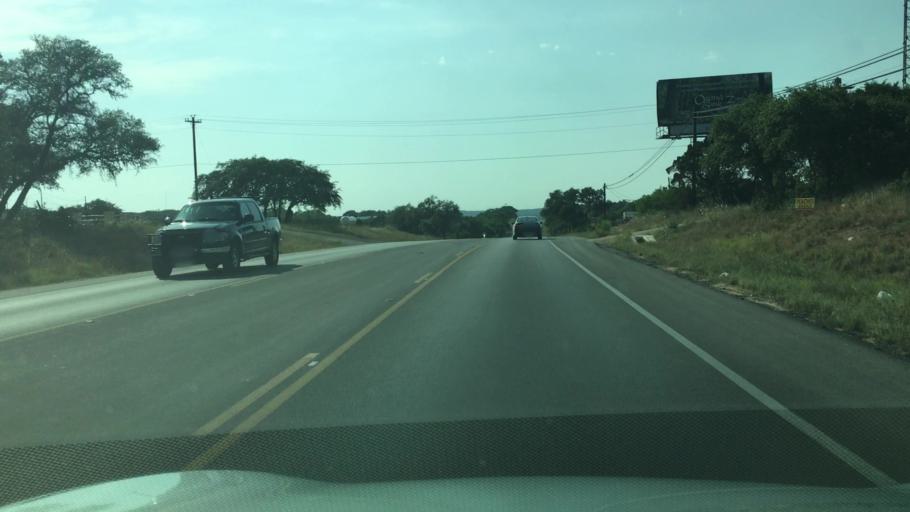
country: US
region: Texas
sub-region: Hays County
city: Wimberley
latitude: 29.9223
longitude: -98.0609
